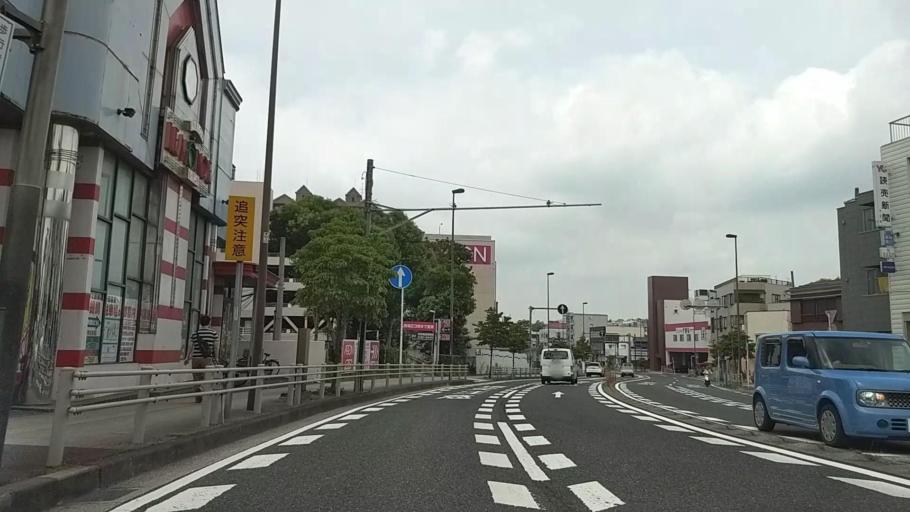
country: JP
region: Kanagawa
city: Yokohama
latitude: 35.4585
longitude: 139.6007
